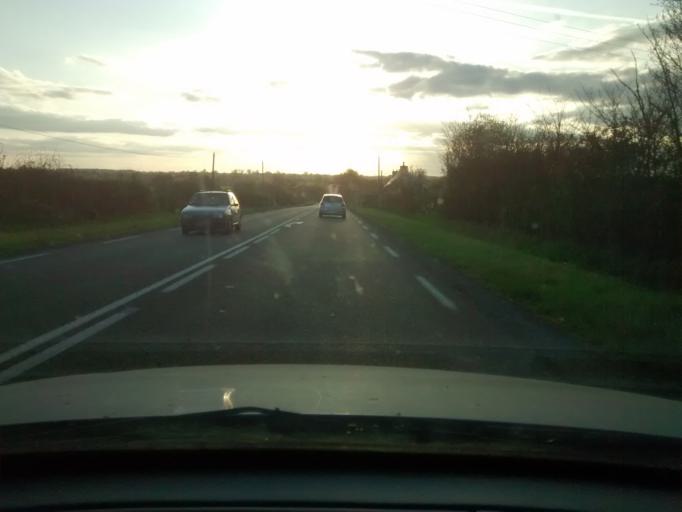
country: FR
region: Pays de la Loire
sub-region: Departement de la Mayenne
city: Sainte-Suzanne
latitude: 48.0337
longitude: -0.3658
